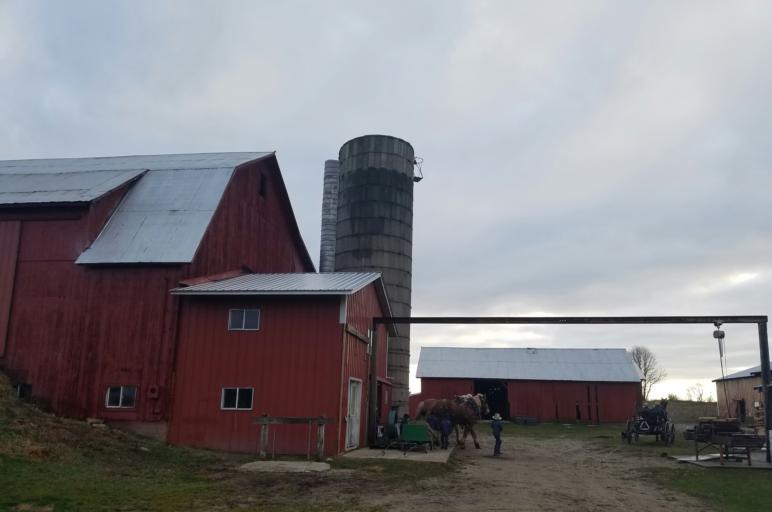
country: US
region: Michigan
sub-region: Mecosta County
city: Canadian Lakes
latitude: 43.5502
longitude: -85.3627
